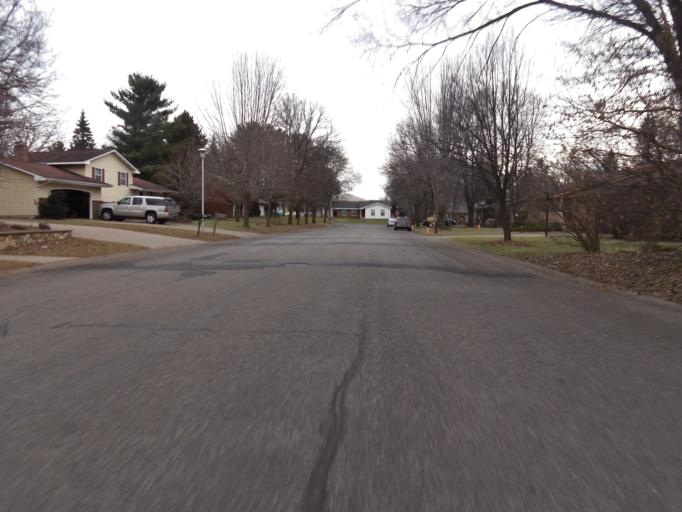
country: US
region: Wisconsin
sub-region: Pierce County
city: River Falls
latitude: 44.8569
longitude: -92.6095
